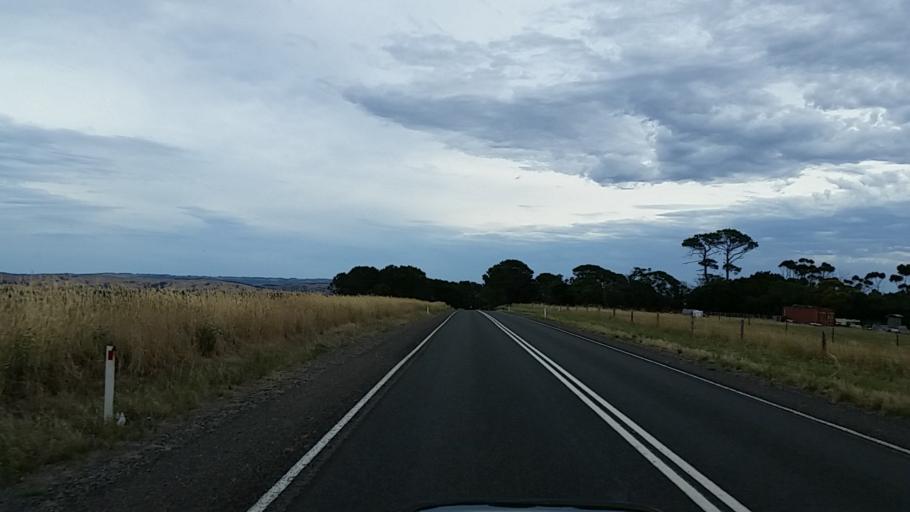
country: AU
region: South Australia
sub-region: Onkaparinga
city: Port Willunga
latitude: -35.3892
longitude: 138.4273
